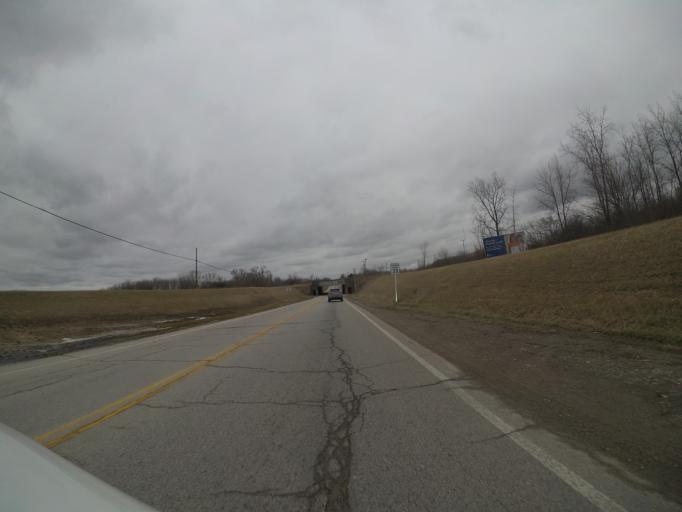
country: US
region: Ohio
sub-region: Wood County
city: Walbridge
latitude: 41.6034
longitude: -83.5122
